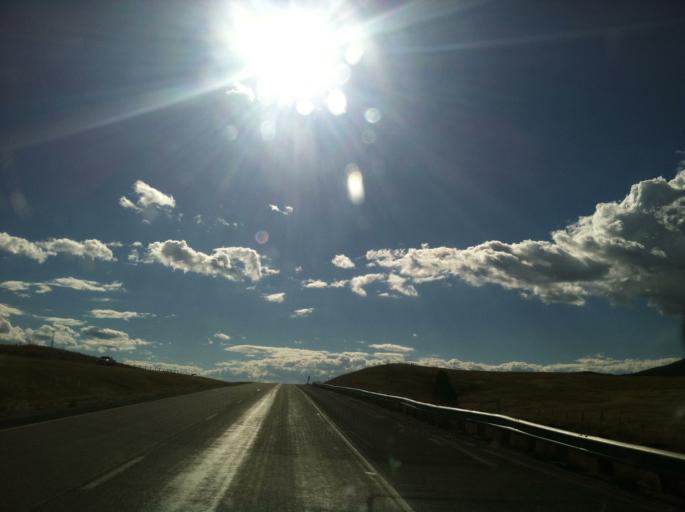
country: US
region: Montana
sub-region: Jefferson County
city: Whitehall
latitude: 45.8922
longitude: -111.8525
